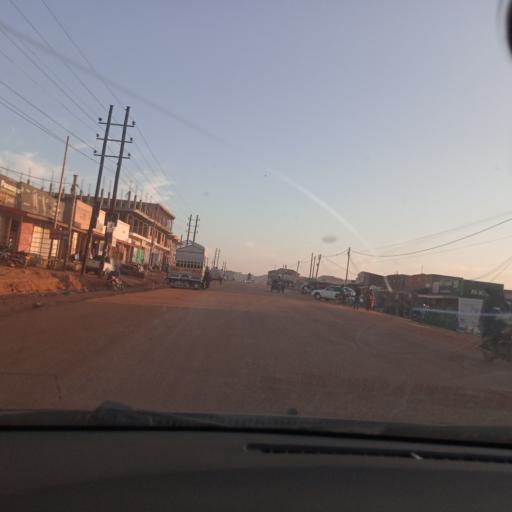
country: UG
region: Central Region
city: Masaka
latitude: -0.3210
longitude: 31.7571
